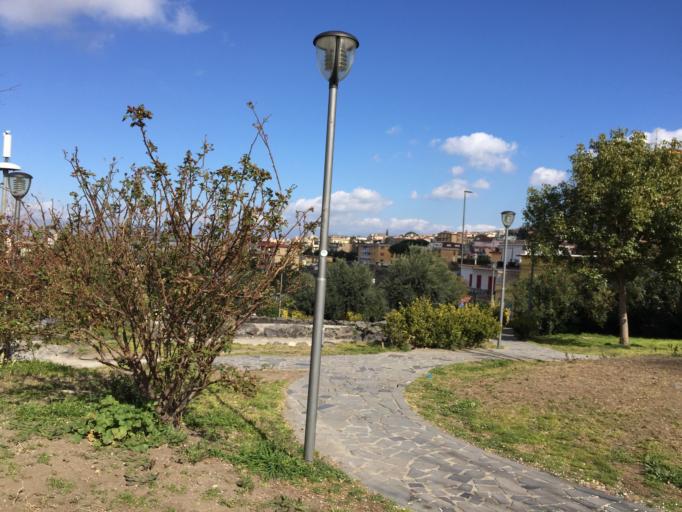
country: IT
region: Campania
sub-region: Provincia di Napoli
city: Massa di Somma
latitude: 40.8495
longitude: 14.3709
